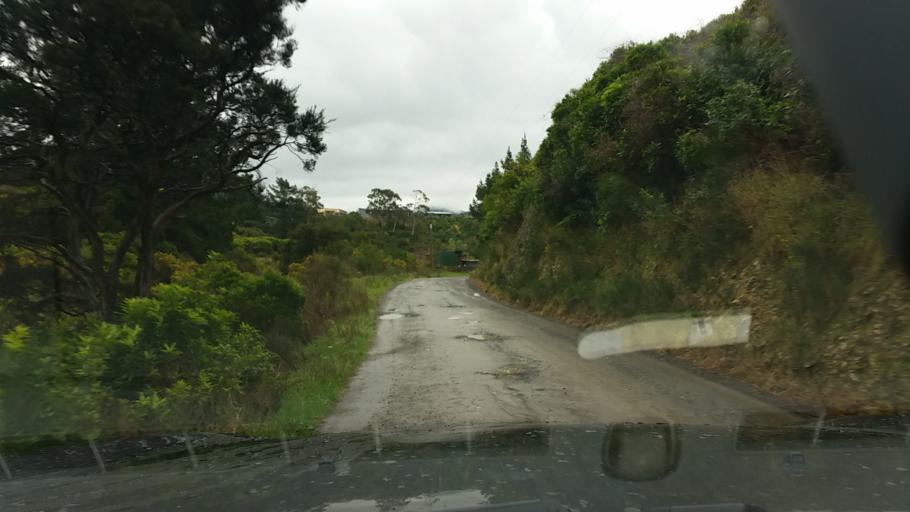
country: NZ
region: Marlborough
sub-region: Marlborough District
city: Picton
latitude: -41.2818
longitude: 174.0322
